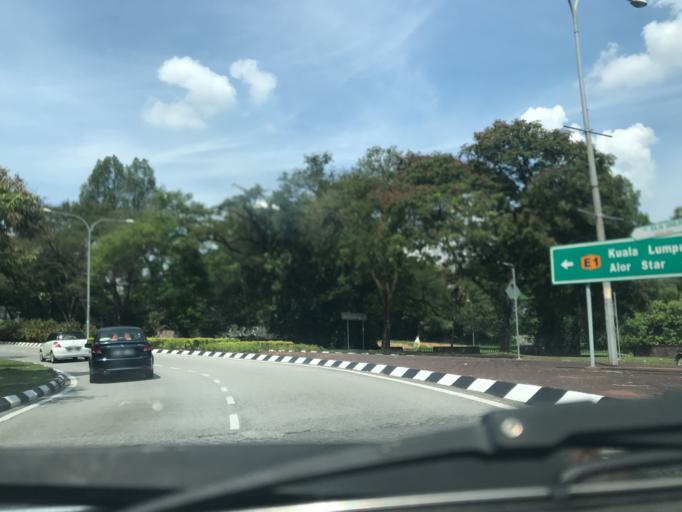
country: MY
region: Perak
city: Ipoh
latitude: 4.5978
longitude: 101.1055
